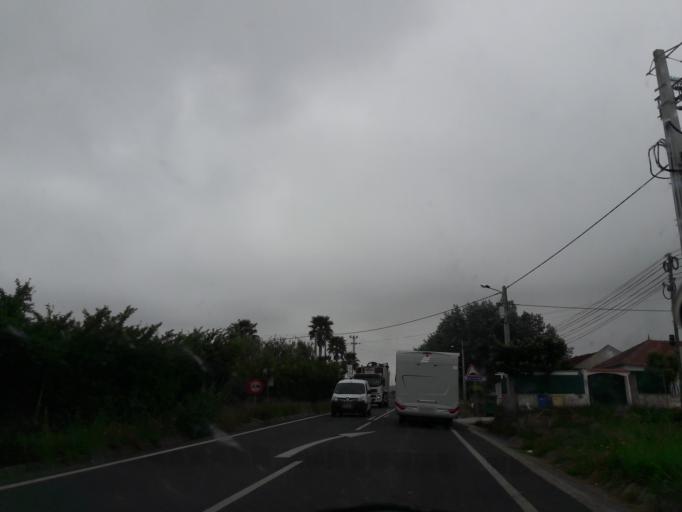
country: PT
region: Leiria
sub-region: Obidos
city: Obidos
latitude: 39.3726
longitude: -9.1407
